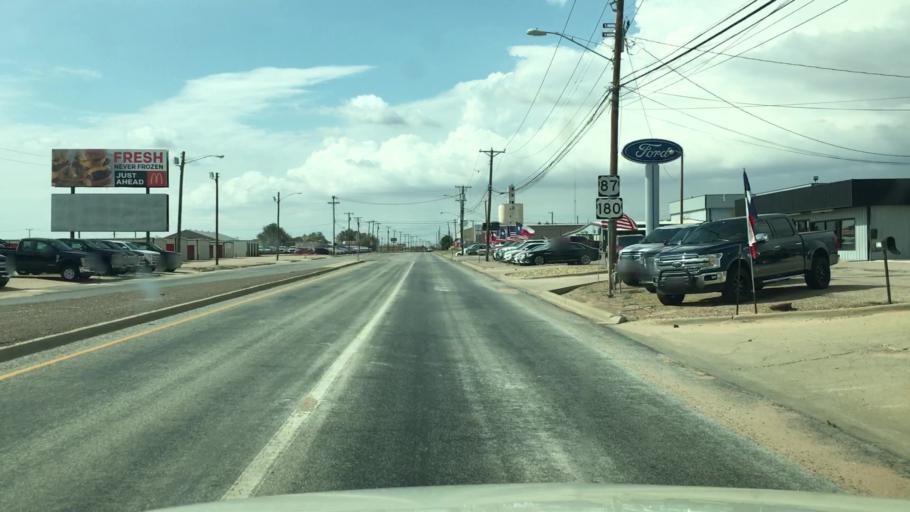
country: US
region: Texas
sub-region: Dawson County
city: Lamesa
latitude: 32.7208
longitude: -101.9453
